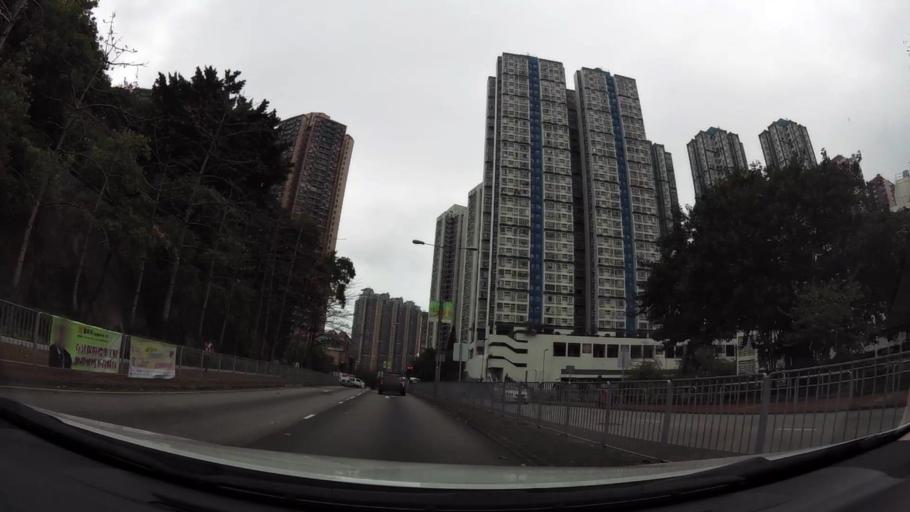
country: HK
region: Tuen Mun
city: Tuen Mun
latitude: 22.4020
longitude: 113.9729
